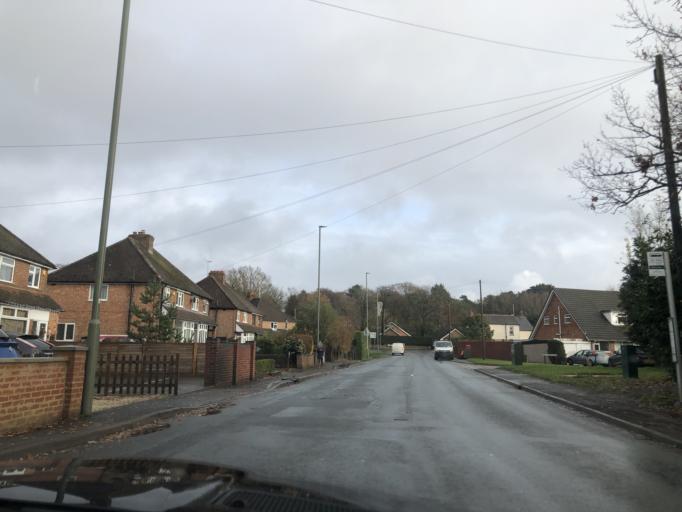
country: GB
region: England
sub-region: Hampshire
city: Farnborough
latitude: 51.2792
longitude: -0.7267
